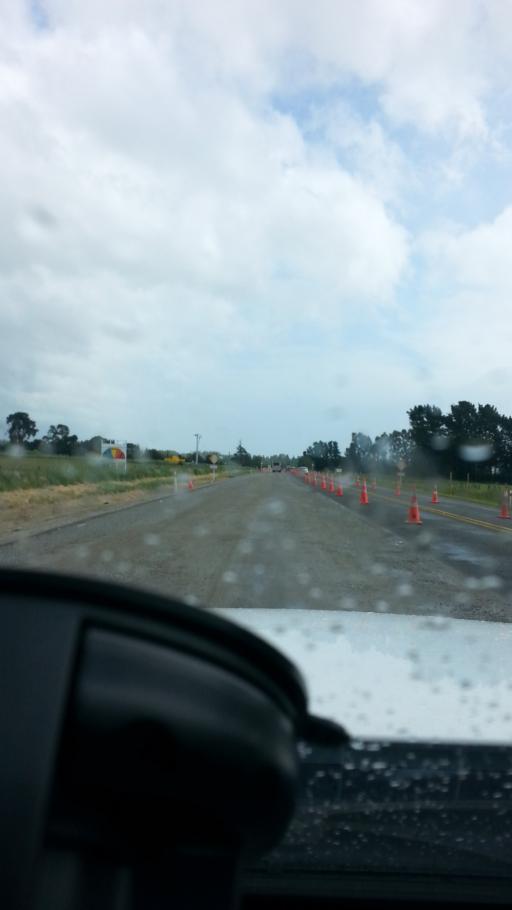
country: NZ
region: Wellington
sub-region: Masterton District
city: Masterton
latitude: -41.0462
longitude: 175.5050
